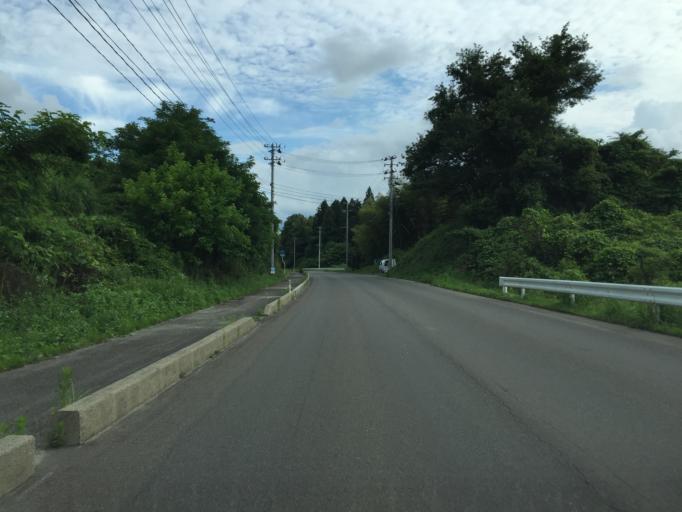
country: JP
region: Fukushima
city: Fukushima-shi
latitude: 37.6883
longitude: 140.5012
